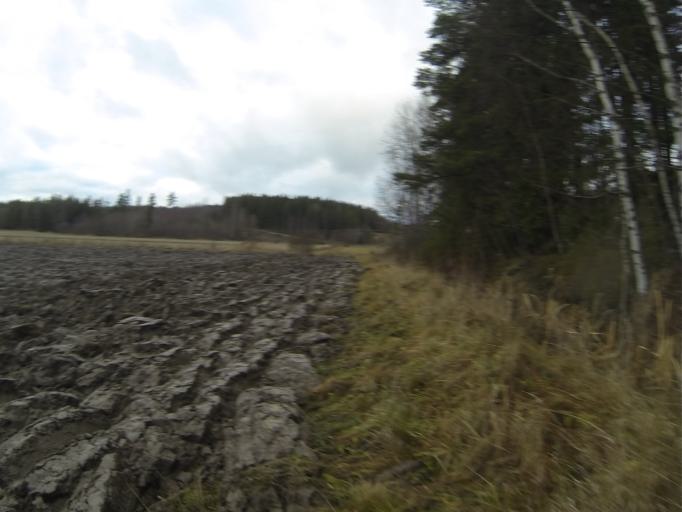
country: FI
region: Varsinais-Suomi
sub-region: Salo
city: Halikko
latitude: 60.4042
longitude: 22.9906
